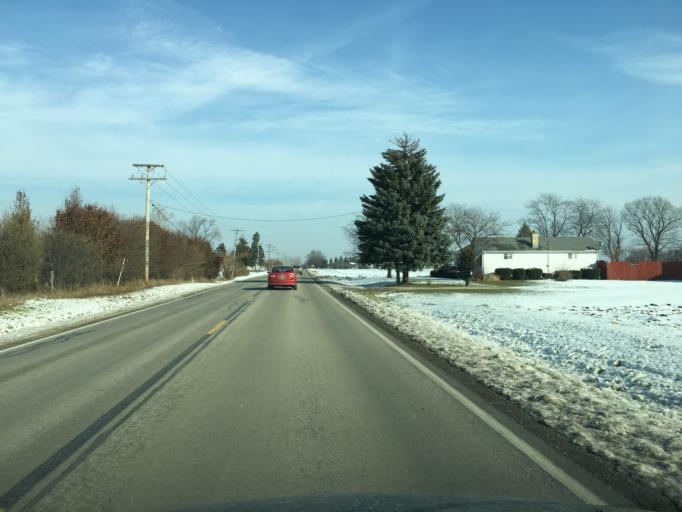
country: US
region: Illinois
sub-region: Will County
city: Plainfield
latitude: 41.6756
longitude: -88.1711
